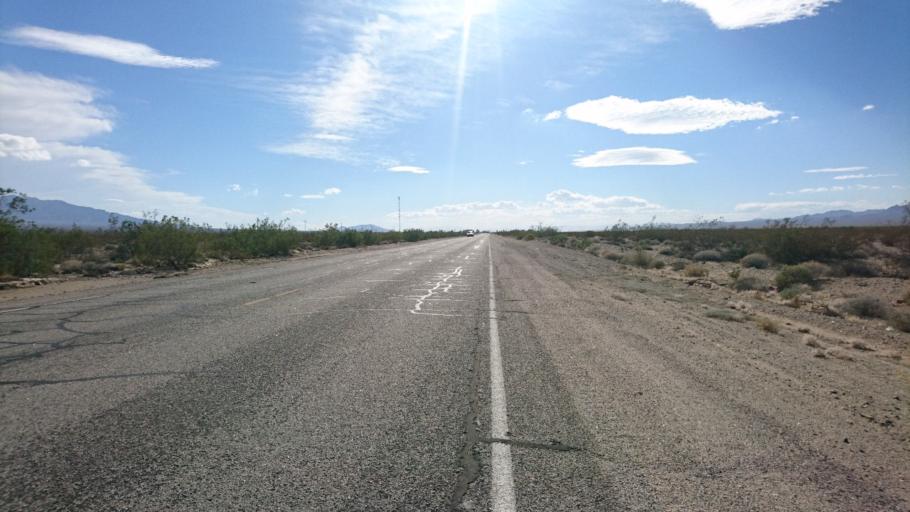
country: US
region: California
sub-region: San Bernardino County
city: Needles
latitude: 34.7435
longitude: -115.2371
